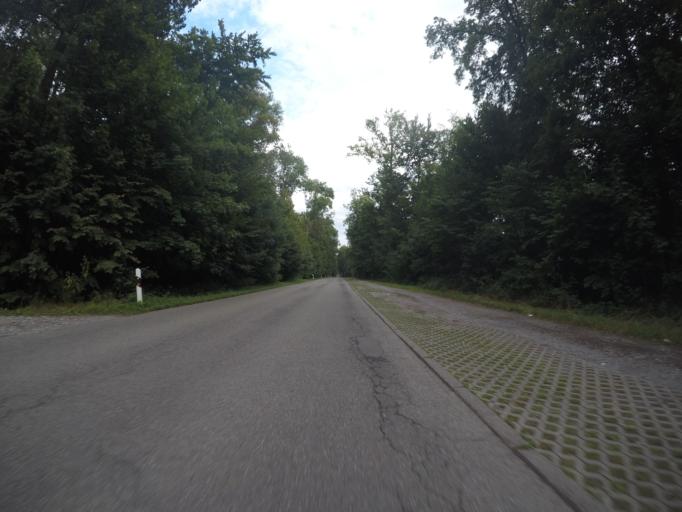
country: DE
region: Baden-Wuerttemberg
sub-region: Regierungsbezirk Stuttgart
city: Stuttgart
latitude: 48.7480
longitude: 9.1877
